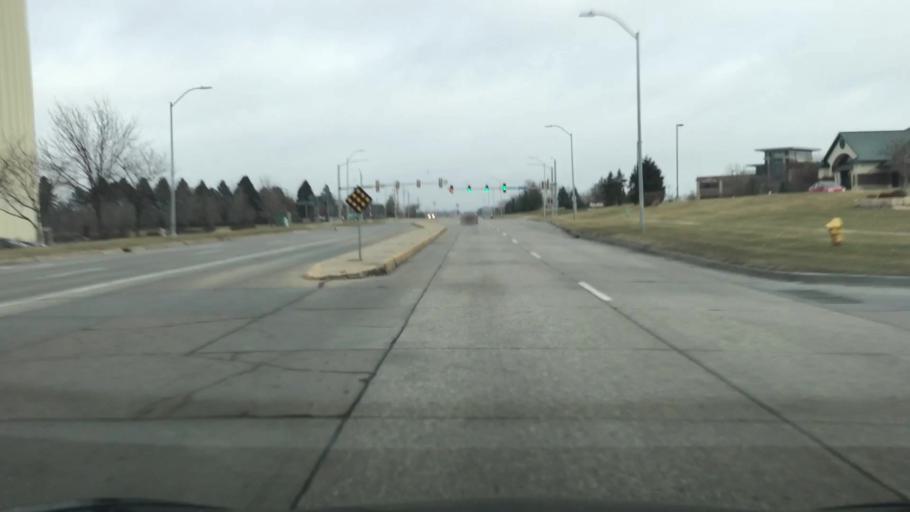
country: US
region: Iowa
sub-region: Polk County
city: Clive
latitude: 41.6004
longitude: -93.7925
